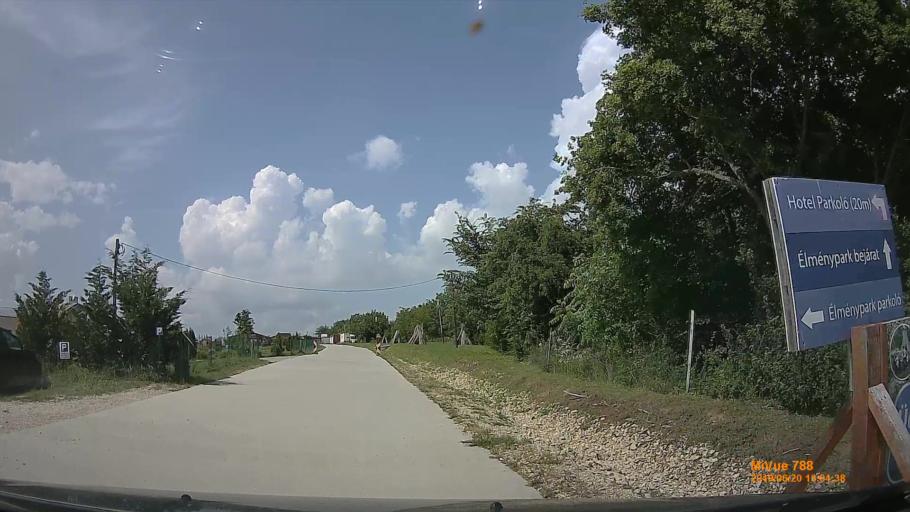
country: HU
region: Baranya
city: Kozarmisleny
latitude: 45.9918
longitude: 18.2605
